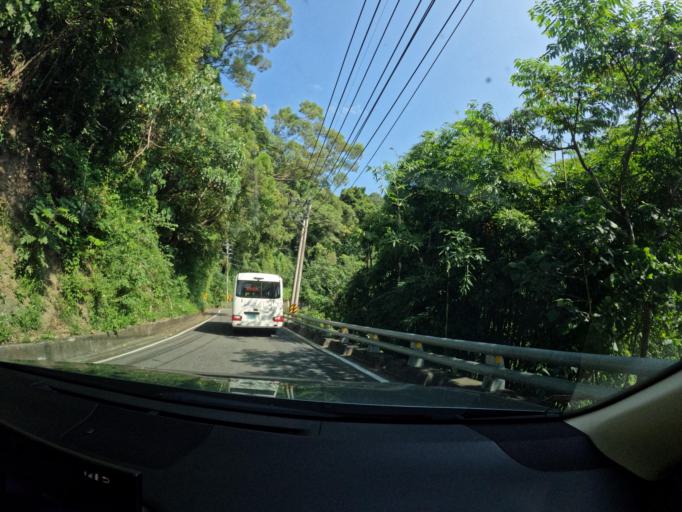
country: TW
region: Taiwan
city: Yujing
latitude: 23.0704
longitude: 120.6390
